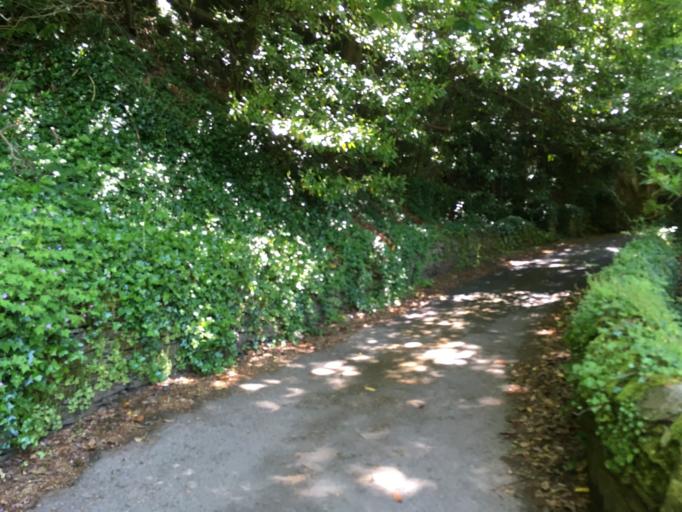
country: GB
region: England
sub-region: Devon
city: Dartmouth
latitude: 50.3469
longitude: -3.5660
